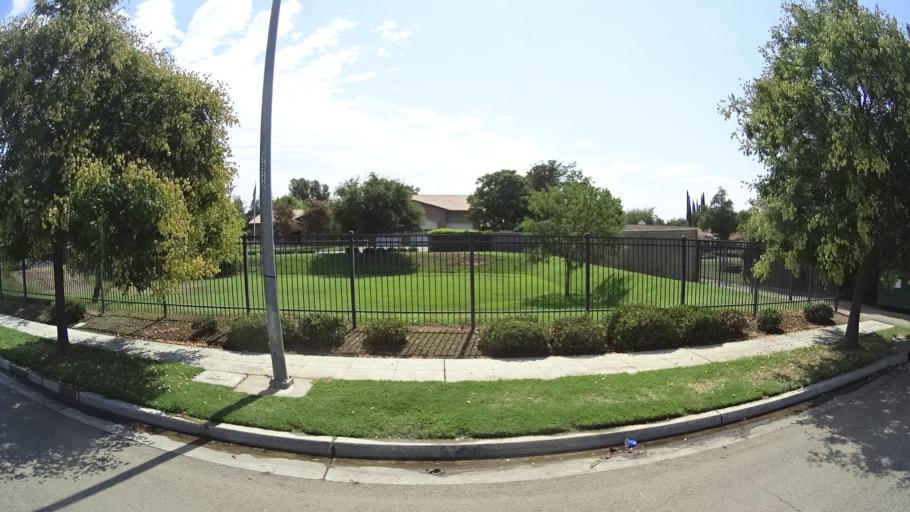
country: US
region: California
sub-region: Fresno County
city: Sunnyside
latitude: 36.7307
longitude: -119.6999
